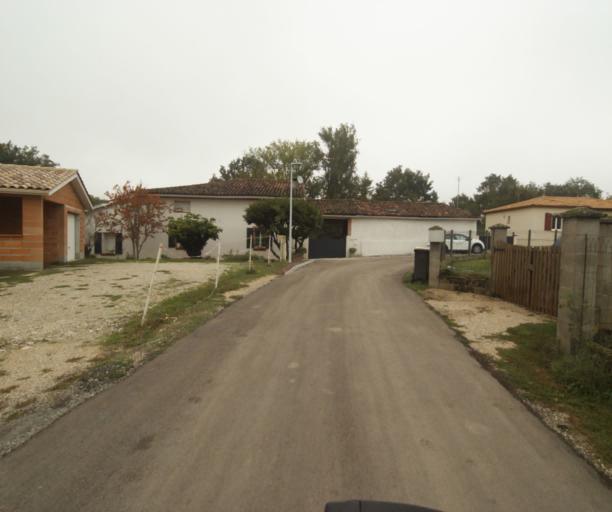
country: FR
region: Midi-Pyrenees
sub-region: Departement du Tarn-et-Garonne
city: Orgueil
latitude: 43.9061
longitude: 1.4136
